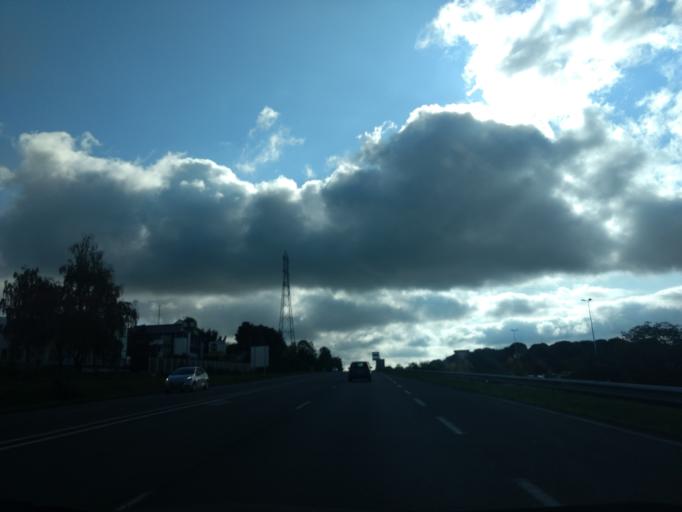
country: FR
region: Poitou-Charentes
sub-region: Departement de la Vienne
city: Chasseneuil-du-Poitou
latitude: 46.6653
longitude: 0.3717
